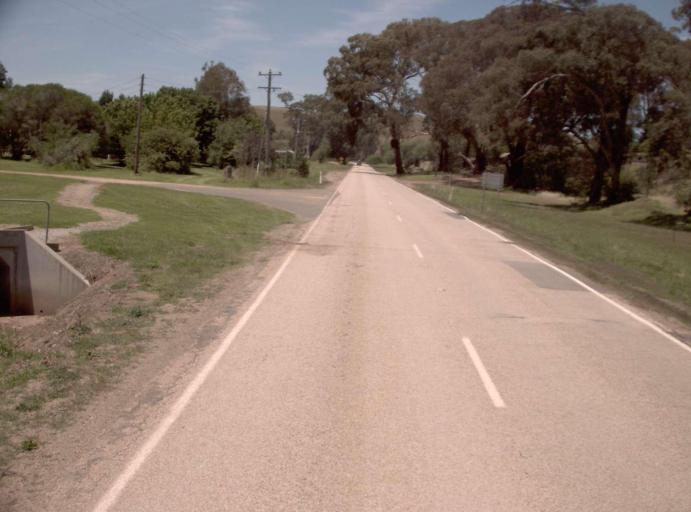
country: AU
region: Victoria
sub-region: East Gippsland
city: Bairnsdale
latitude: -37.2723
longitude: 147.7268
